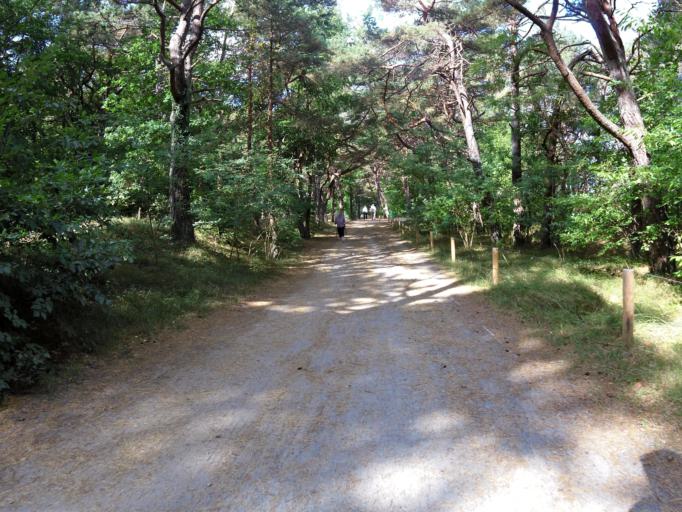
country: DE
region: Mecklenburg-Vorpommern
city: Ostseebad Zinnowitz
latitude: 54.0851
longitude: 13.9047
